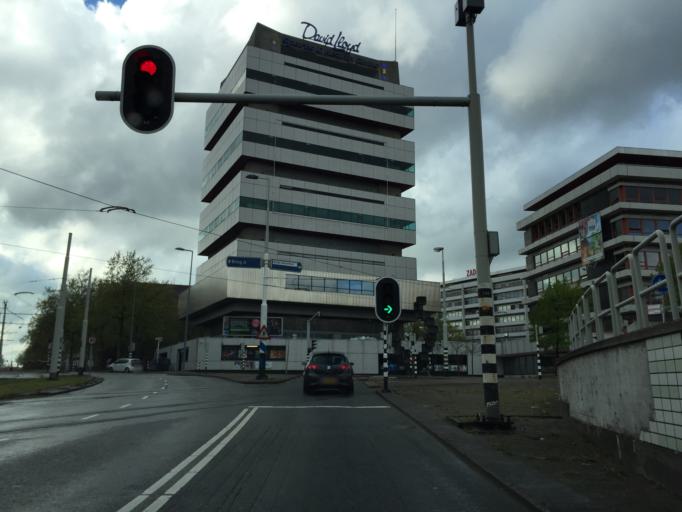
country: NL
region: South Holland
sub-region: Gemeente Rotterdam
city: Rotterdam
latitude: 51.9264
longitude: 4.4768
